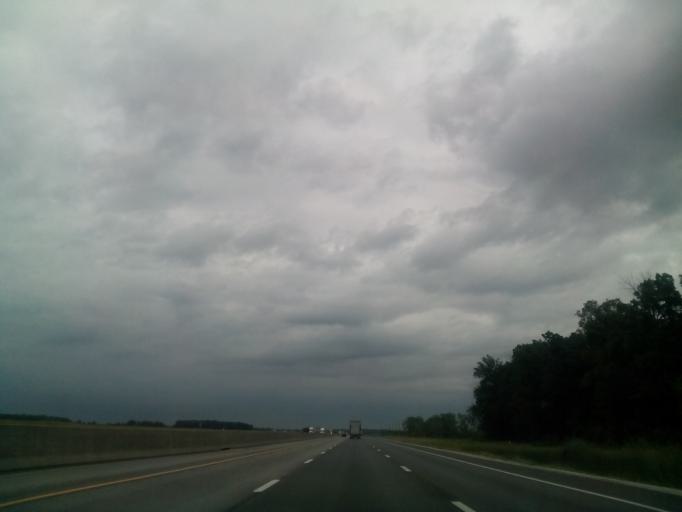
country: US
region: Ohio
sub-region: Sandusky County
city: Woodville
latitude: 41.4829
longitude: -83.3526
